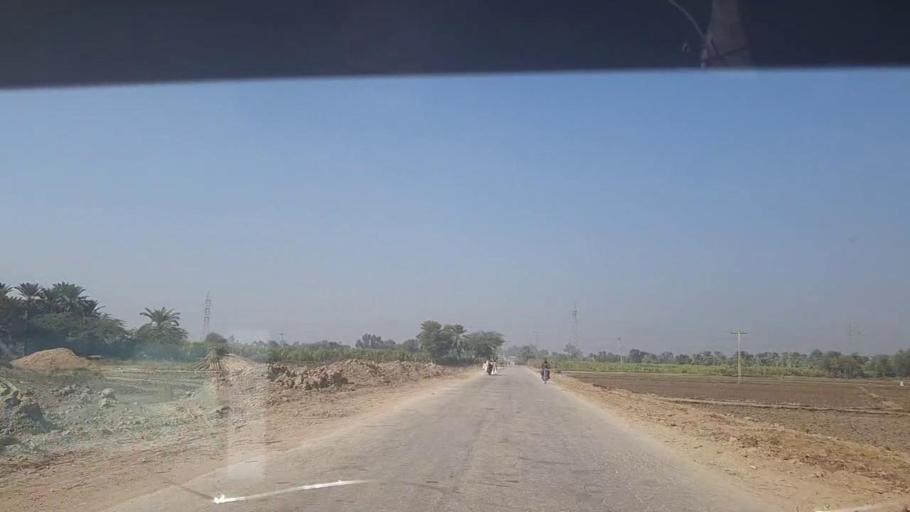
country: PK
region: Sindh
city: Kot Diji
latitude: 27.4257
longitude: 68.6567
